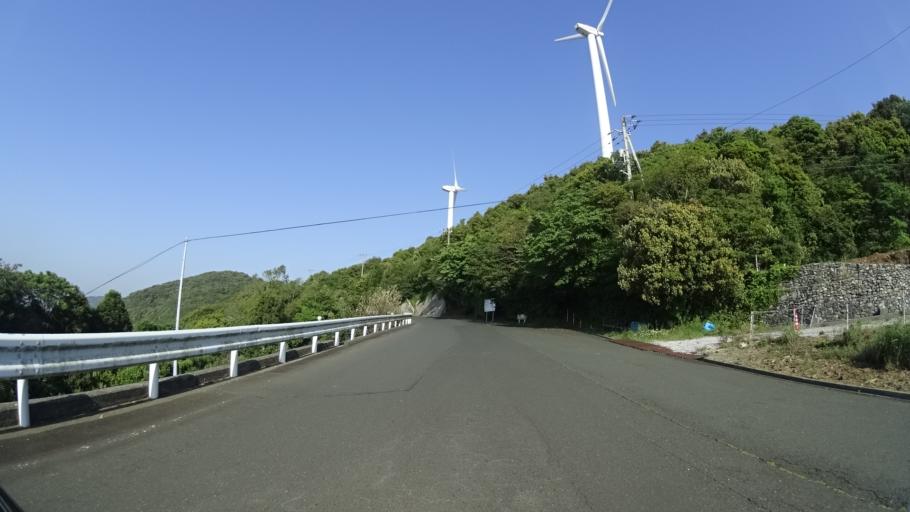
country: JP
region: Ehime
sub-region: Nishiuwa-gun
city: Ikata-cho
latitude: 33.3739
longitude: 132.0616
